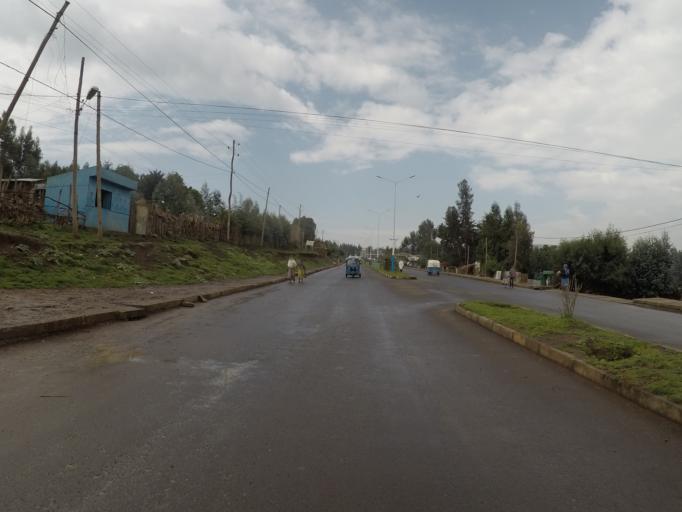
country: ET
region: Amhara
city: Debark'
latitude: 13.1483
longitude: 37.8946
